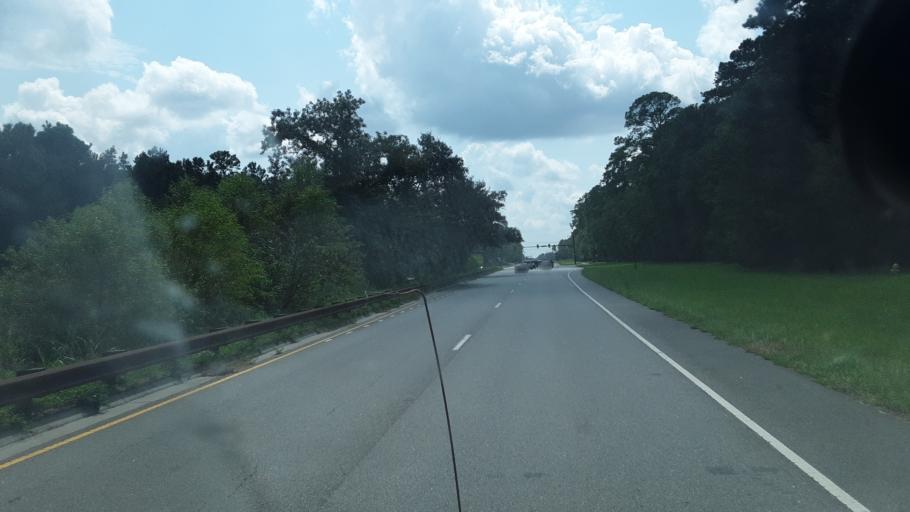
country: US
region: South Carolina
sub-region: Beaufort County
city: Bluffton
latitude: 32.2724
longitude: -80.9507
